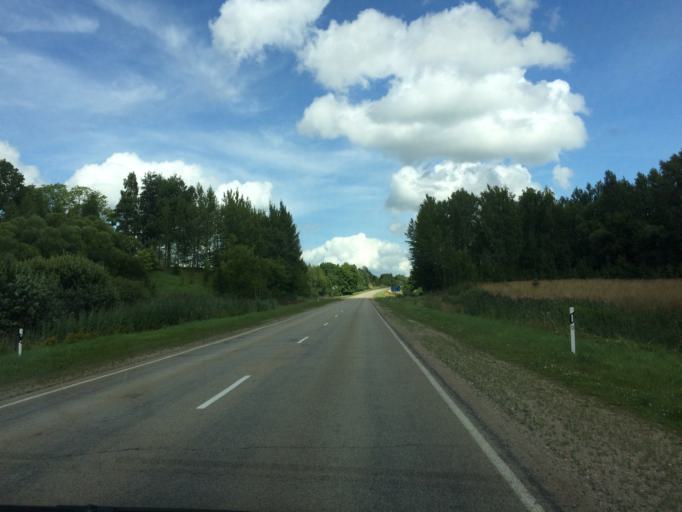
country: LV
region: Rezekne
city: Rezekne
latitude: 56.5754
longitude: 27.3779
